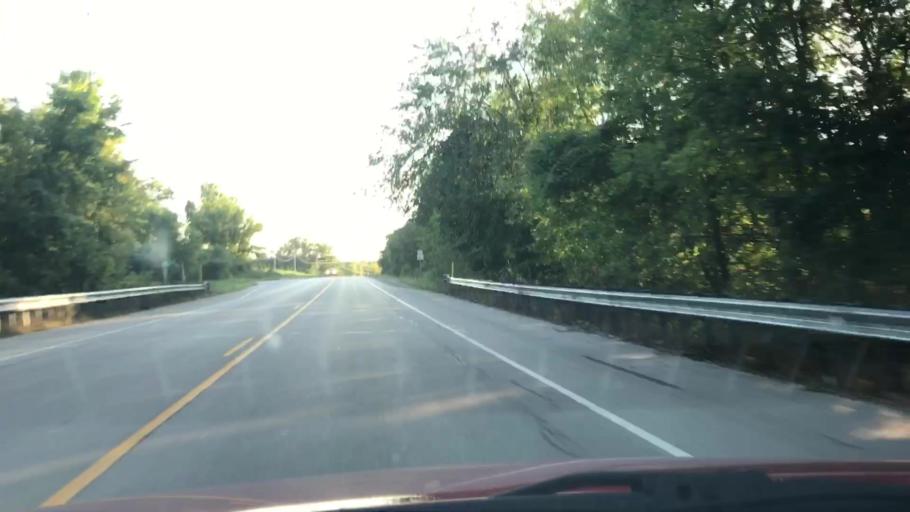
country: US
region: Wisconsin
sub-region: Brown County
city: Oneida
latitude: 44.5141
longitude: -88.1462
